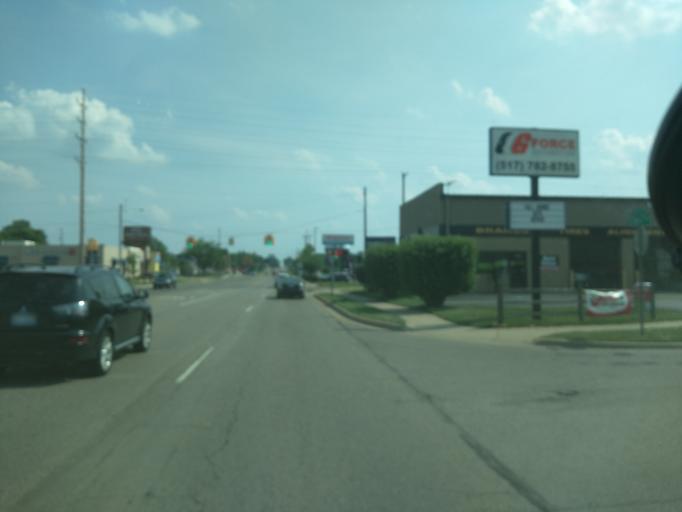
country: US
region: Michigan
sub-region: Jackson County
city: Jackson
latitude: 42.2659
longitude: -84.4234
